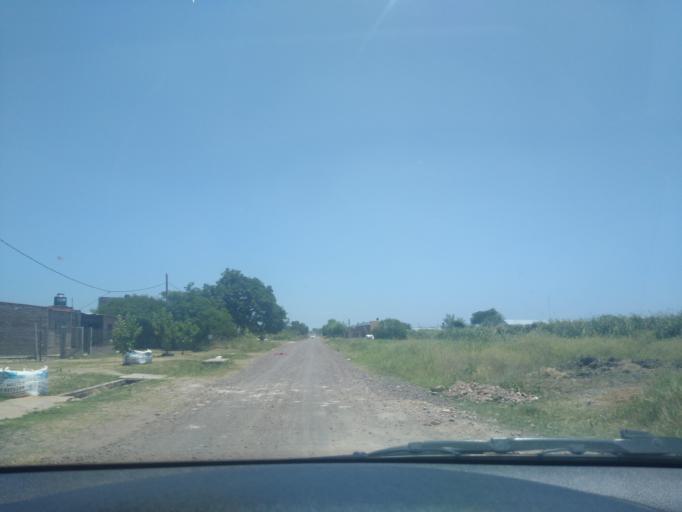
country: AR
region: Chaco
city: Puerto Tirol
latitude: -27.3824
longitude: -59.0921
